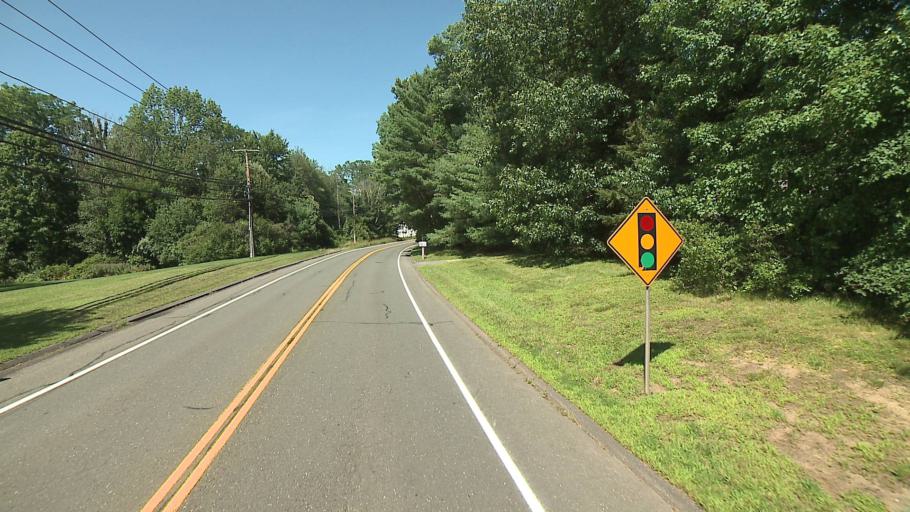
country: US
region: Connecticut
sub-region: Hartford County
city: Weatogue
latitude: 41.8391
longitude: -72.8519
